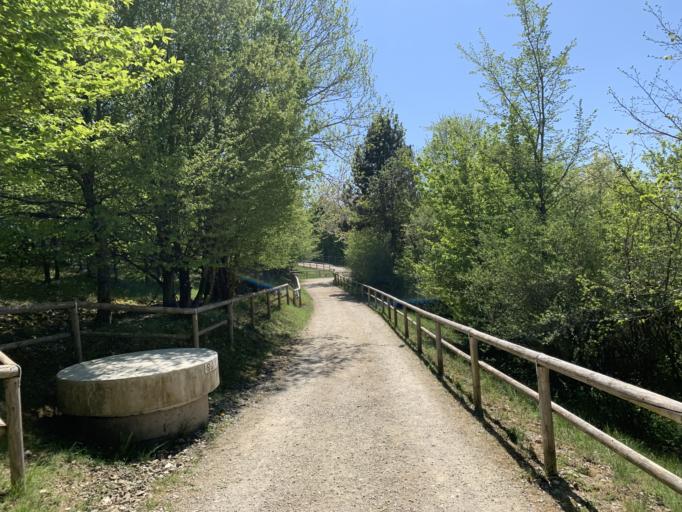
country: DE
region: Bavaria
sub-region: Swabia
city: Gersthofen
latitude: 48.4183
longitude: 10.8930
